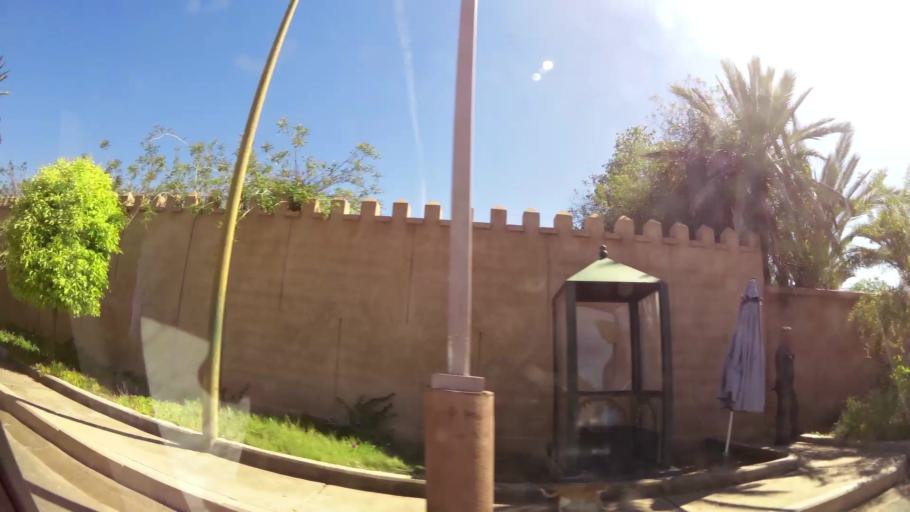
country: MA
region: Marrakech-Tensift-Al Haouz
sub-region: Marrakech
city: Marrakesh
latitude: 31.6564
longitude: -7.9597
